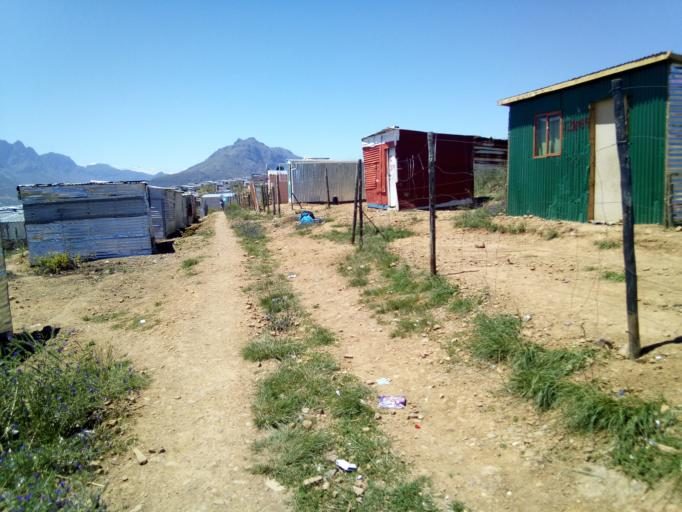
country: ZA
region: Western Cape
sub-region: Cape Winelands District Municipality
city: Stellenbosch
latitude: -33.9210
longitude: 18.8352
